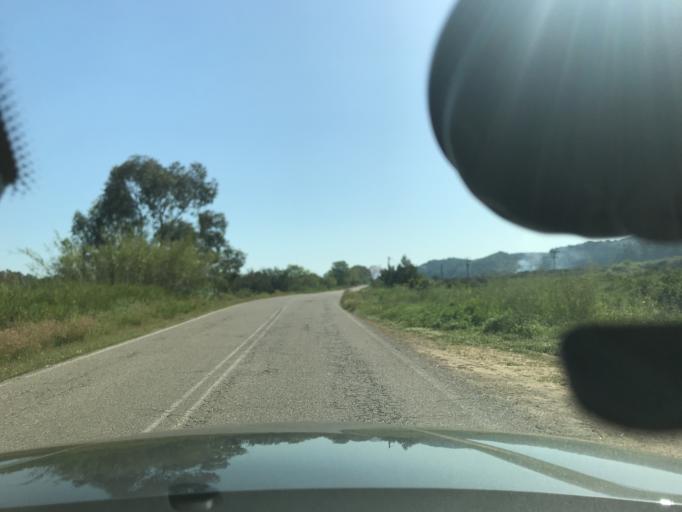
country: GR
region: West Greece
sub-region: Nomos Ileias
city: Epitalion
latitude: 37.6399
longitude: 21.4858
